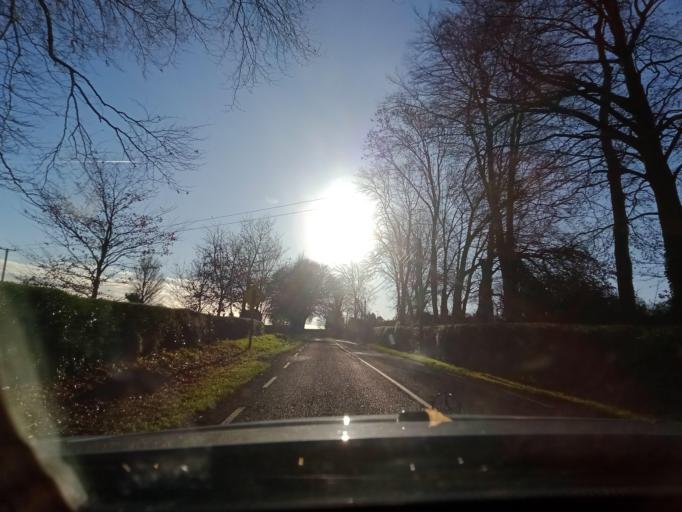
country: IE
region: Leinster
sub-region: Kilkenny
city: Piltown
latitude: 52.3756
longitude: -7.3399
